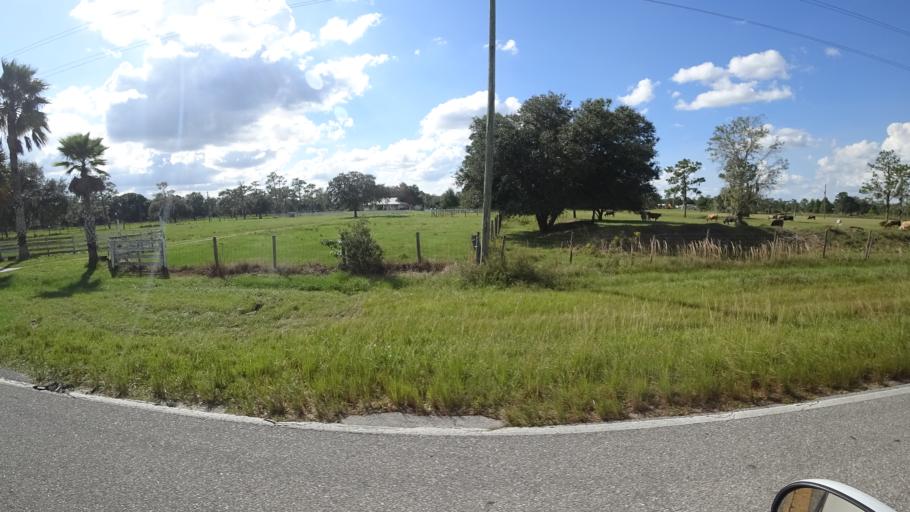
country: US
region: Florida
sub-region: Sarasota County
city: Warm Mineral Springs
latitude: 27.2754
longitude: -82.1157
